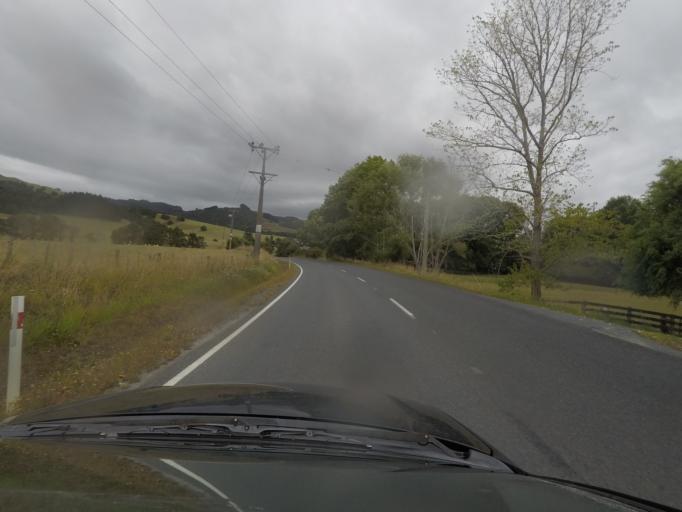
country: NZ
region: Auckland
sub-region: Auckland
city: Warkworth
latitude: -36.2869
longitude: 174.6614
